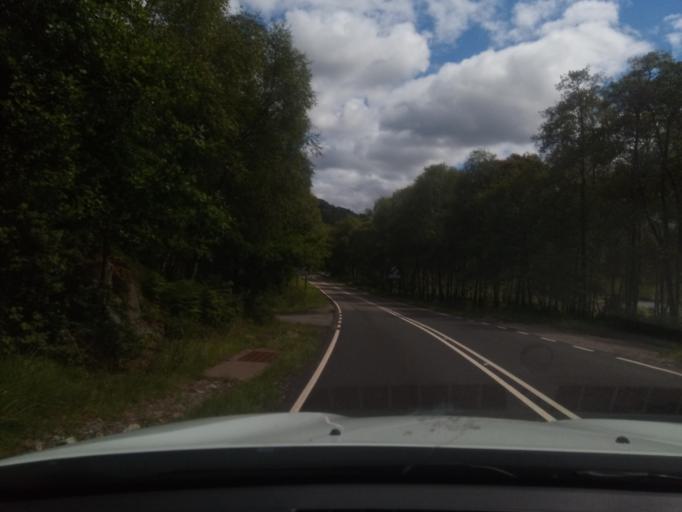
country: GB
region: Scotland
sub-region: Highland
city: Fort William
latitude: 56.8683
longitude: -5.4328
